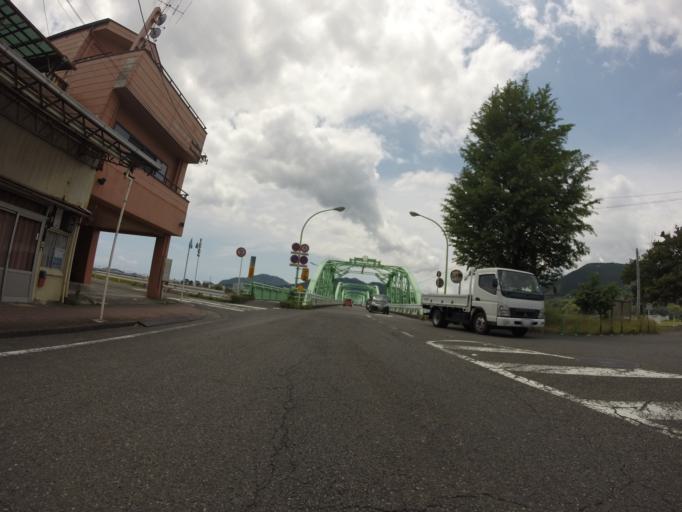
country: JP
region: Shizuoka
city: Shizuoka-shi
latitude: 34.9618
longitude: 138.3696
